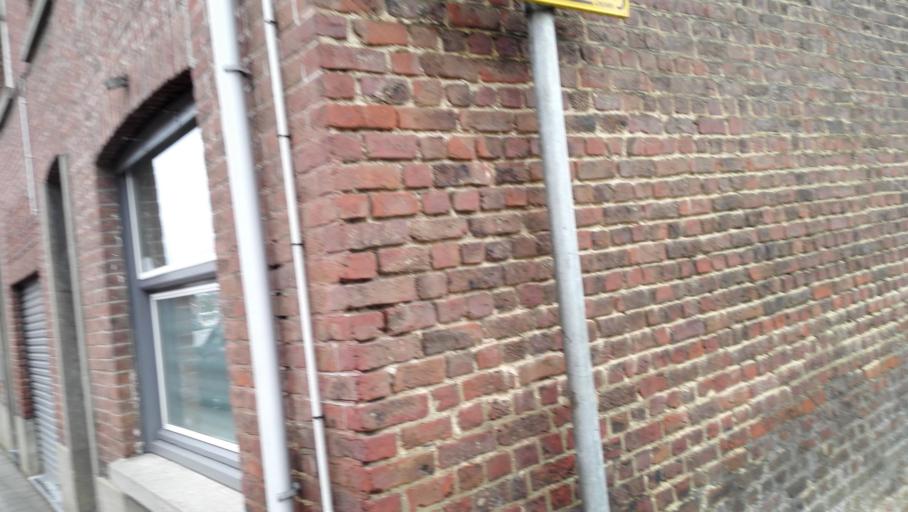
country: BE
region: Flanders
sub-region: Provincie Vlaams-Brabant
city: Holsbeek
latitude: 50.8984
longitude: 4.7326
